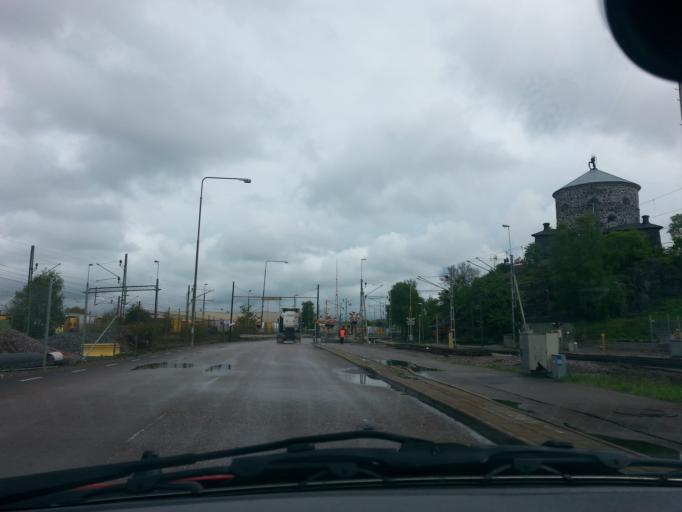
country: SE
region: Vaestra Goetaland
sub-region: Goteborg
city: Goeteborg
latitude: 57.7139
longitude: 11.9869
